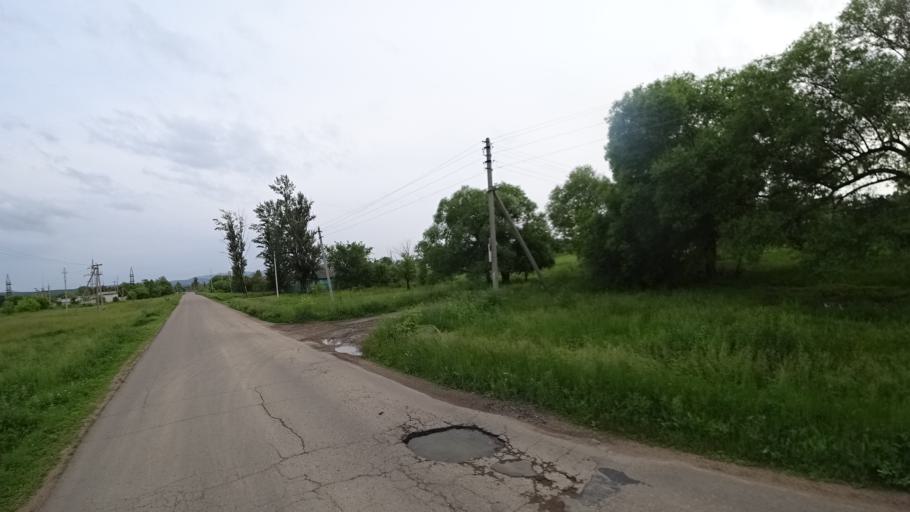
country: RU
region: Primorskiy
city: Novosysoyevka
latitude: 44.2359
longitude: 133.3699
